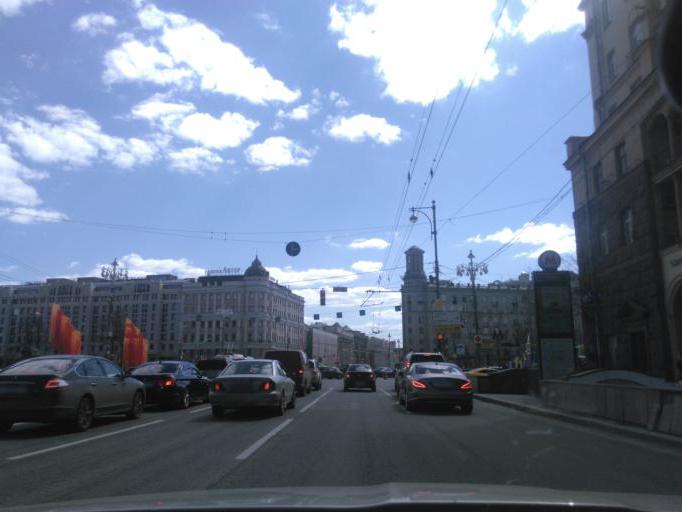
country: RU
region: Moscow
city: Moscow
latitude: 55.7656
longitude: 37.6036
